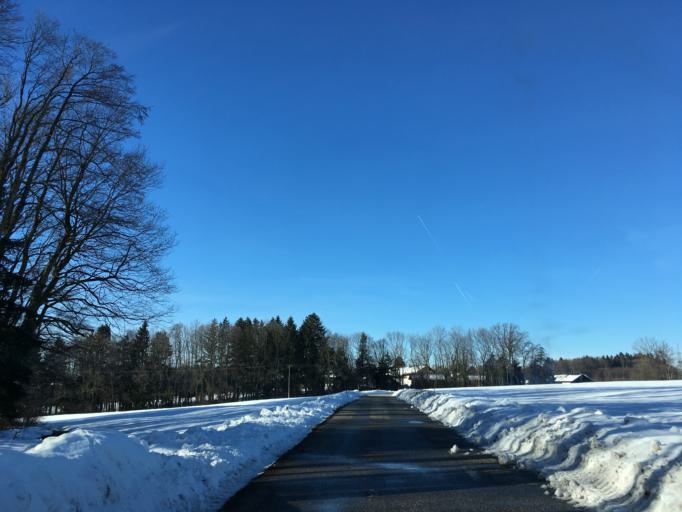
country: DE
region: Bavaria
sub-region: Upper Bavaria
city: Bernau am Chiemsee
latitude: 47.8127
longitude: 12.3386
